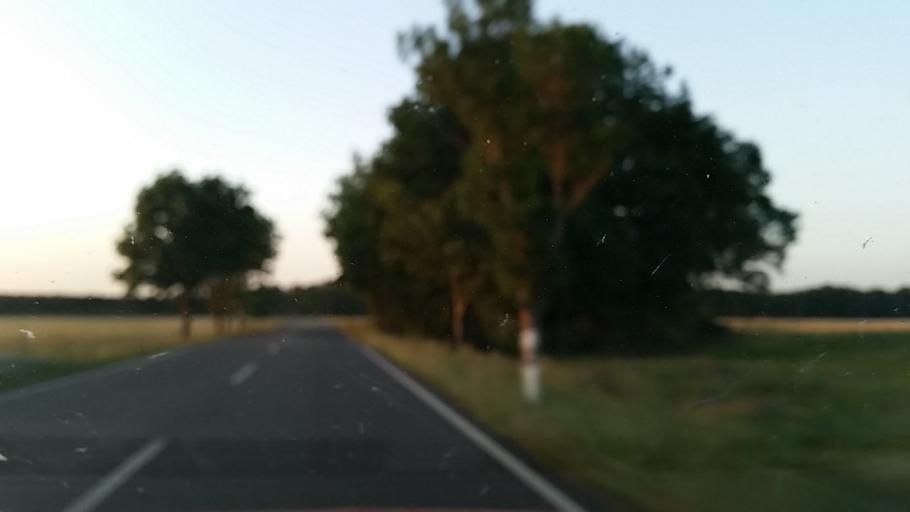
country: DE
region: Saxony-Anhalt
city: Jessen
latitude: 51.7658
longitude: 12.9493
